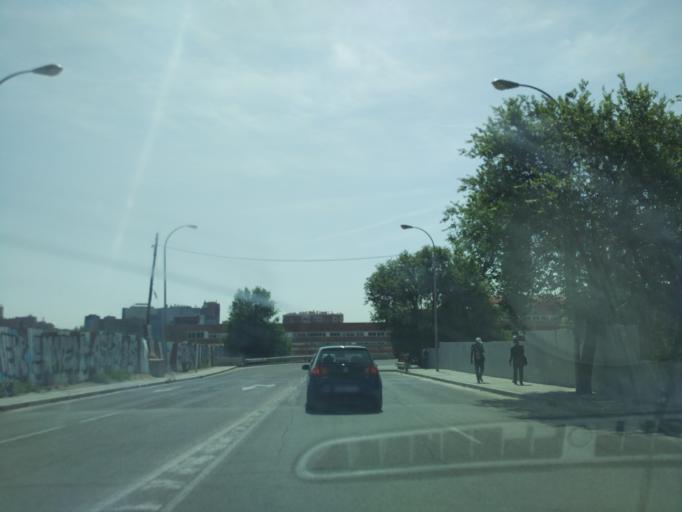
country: ES
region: Madrid
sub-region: Provincia de Madrid
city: Chamartin
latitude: 40.4738
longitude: -3.6849
